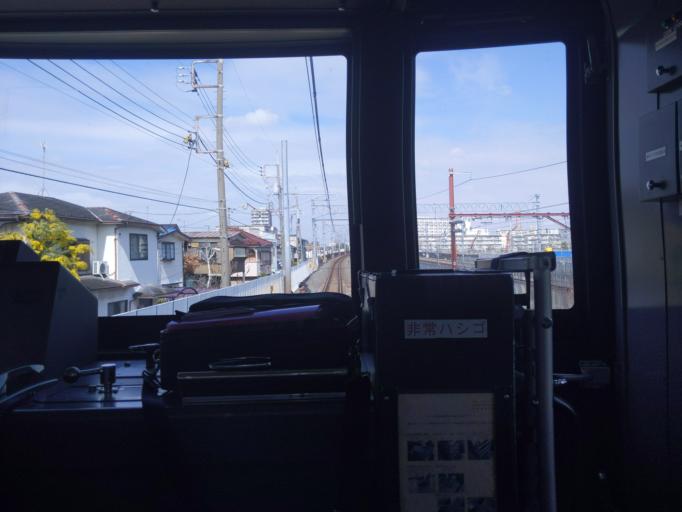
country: JP
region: Saitama
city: Soka
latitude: 35.7976
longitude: 139.7918
